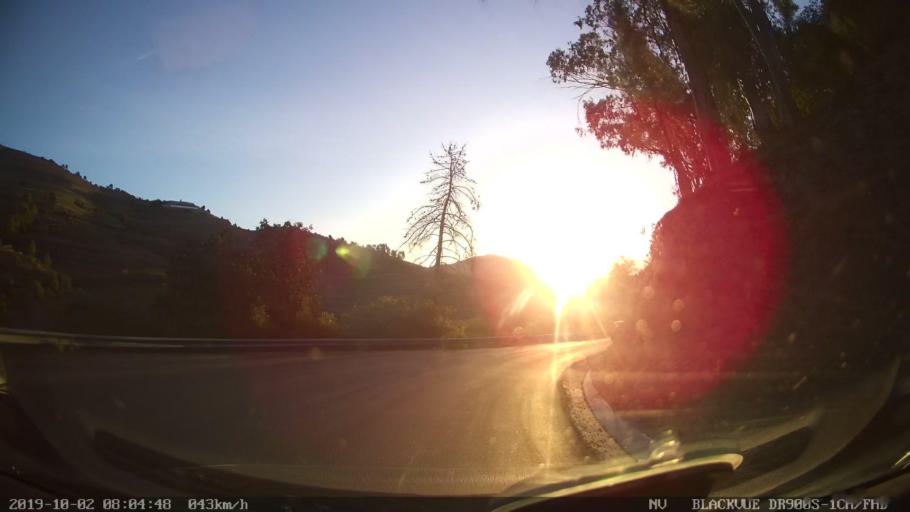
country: PT
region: Vila Real
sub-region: Sabrosa
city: Vilela
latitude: 41.2012
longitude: -7.5608
